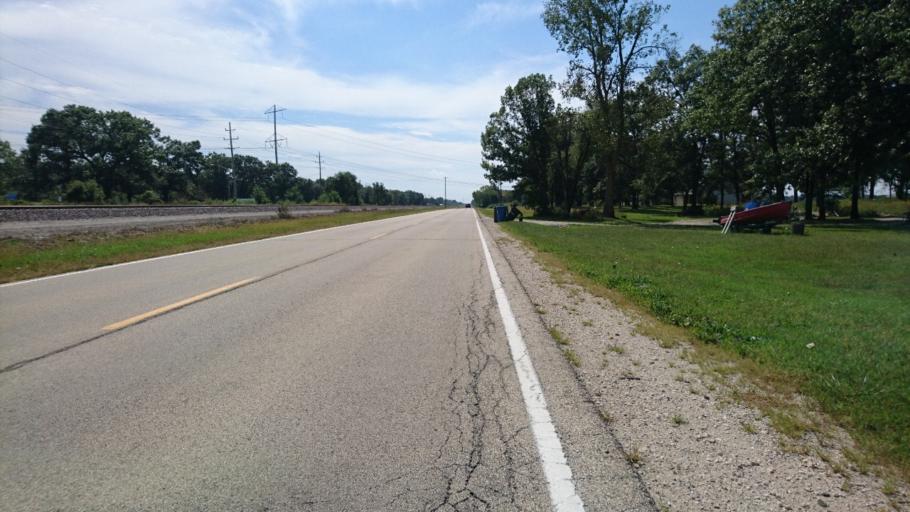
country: US
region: Illinois
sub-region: Will County
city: Braidwood
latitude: 41.2475
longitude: -88.2336
